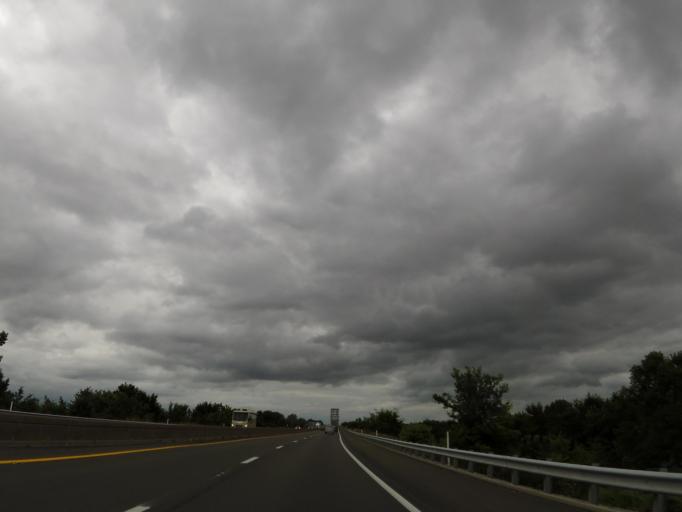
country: US
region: Illinois
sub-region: Massac County
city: Metropolis
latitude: 37.1178
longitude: -88.6927
